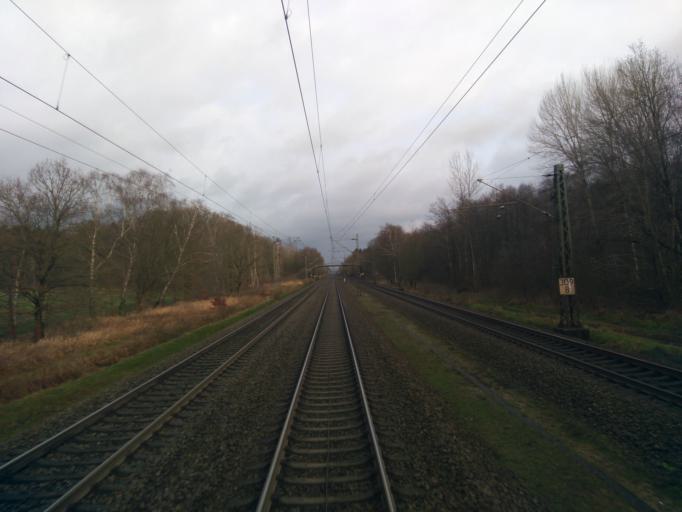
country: DE
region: Lower Saxony
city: Tostedt
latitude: 53.2616
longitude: 9.7095
